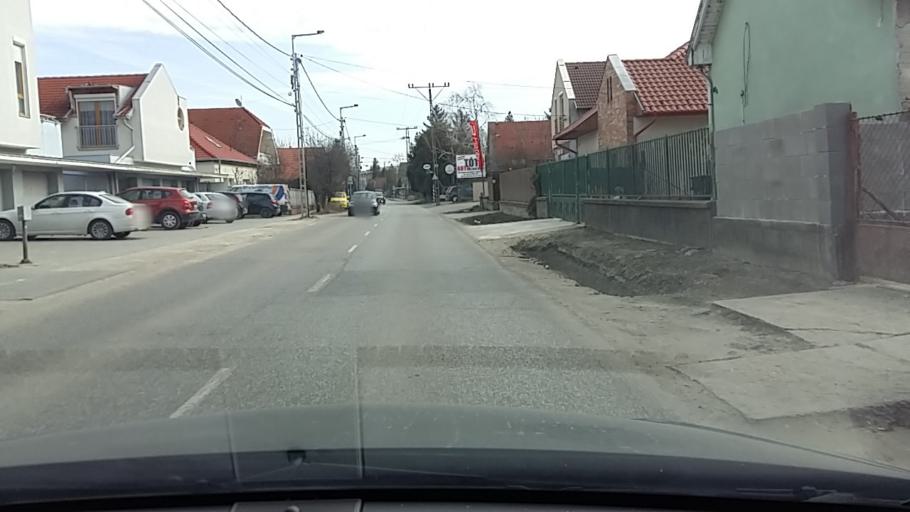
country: HU
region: Pest
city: Szigetszentmiklos
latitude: 47.3445
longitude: 19.0323
